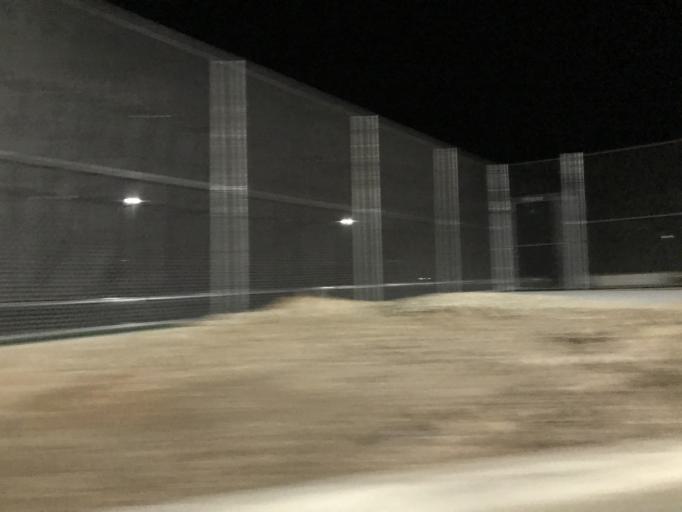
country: US
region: Texas
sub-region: Taylor County
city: Potosi
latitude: 32.3730
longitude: -99.7148
